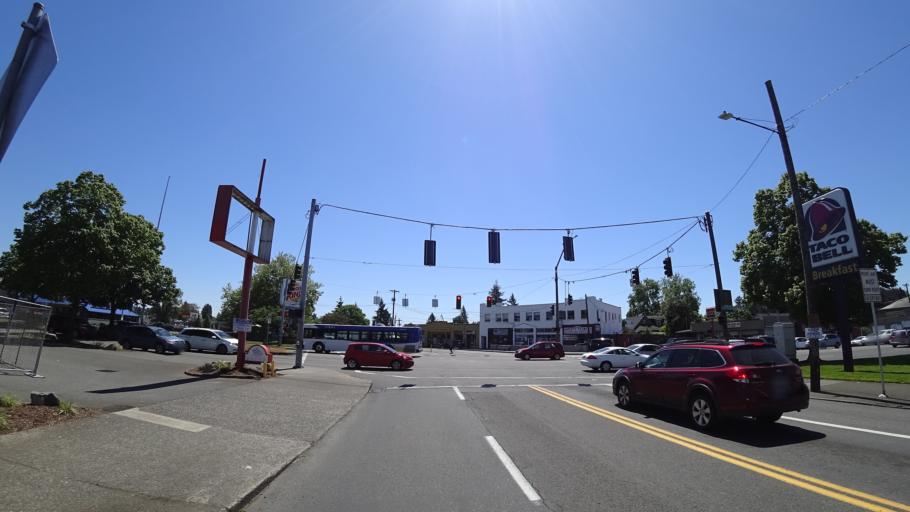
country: US
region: Oregon
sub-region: Multnomah County
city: Lents
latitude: 45.4978
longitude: -122.6113
